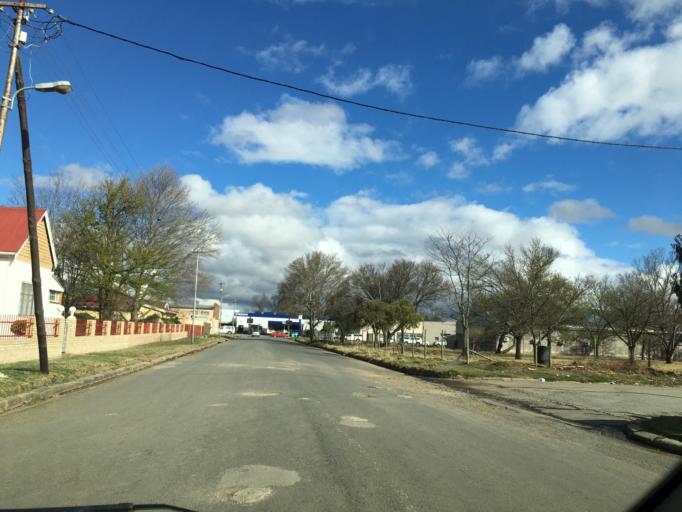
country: ZA
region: Eastern Cape
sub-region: Chris Hani District Municipality
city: Elliot
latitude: -31.3317
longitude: 27.8531
